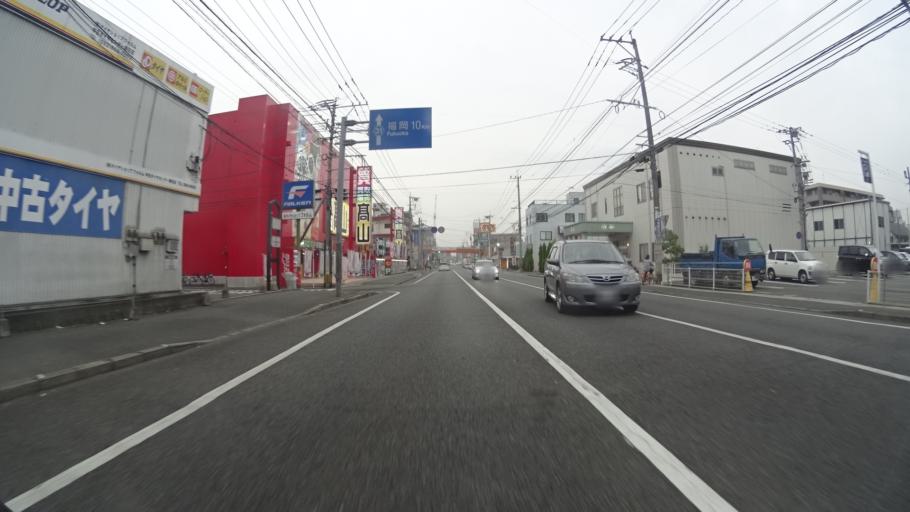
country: JP
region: Fukuoka
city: Onojo
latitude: 33.5409
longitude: 130.4510
